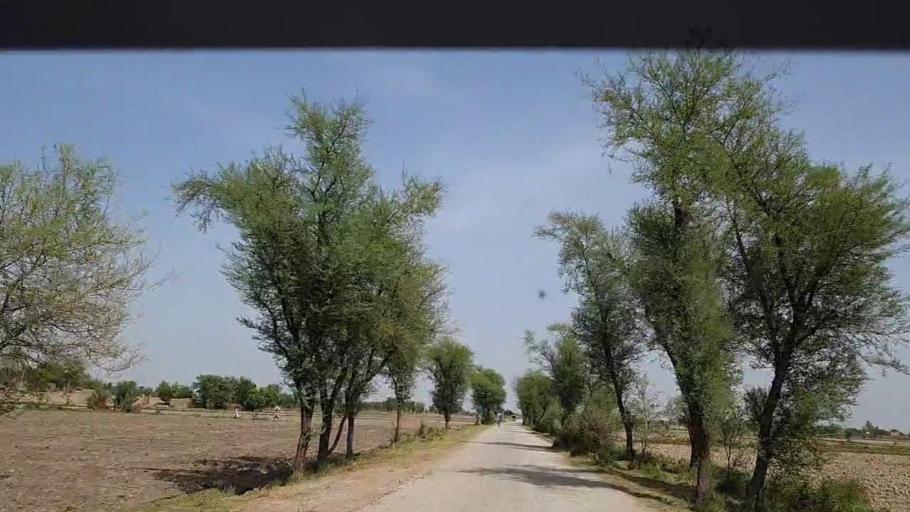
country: PK
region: Sindh
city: Phulji
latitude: 26.9543
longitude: 67.7131
